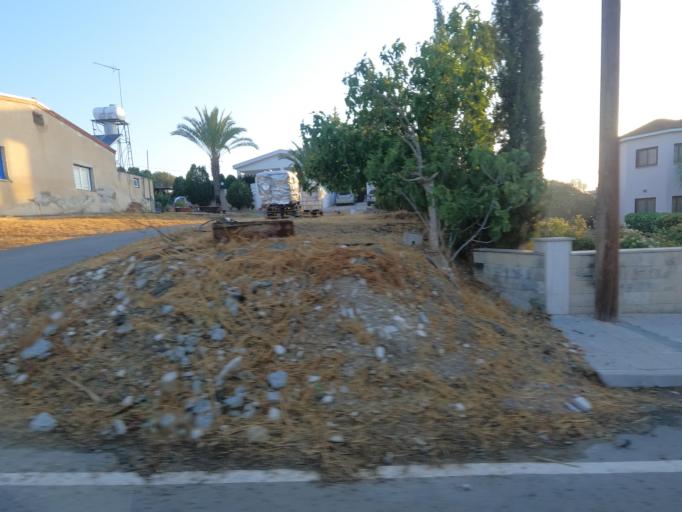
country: CY
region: Lefkosia
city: Alampra
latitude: 34.9880
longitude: 33.4011
